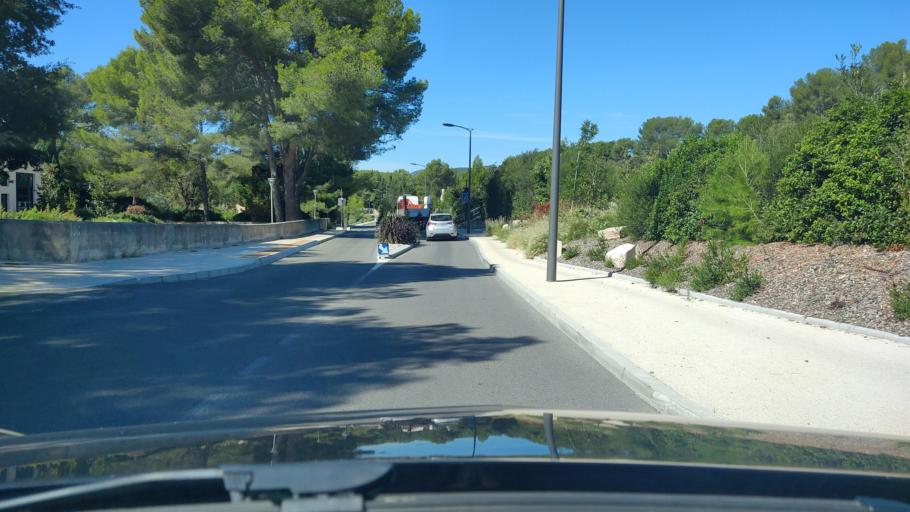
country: FR
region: Provence-Alpes-Cote d'Azur
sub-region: Departement du Var
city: Sanary-sur-Mer
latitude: 43.1414
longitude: 5.7798
